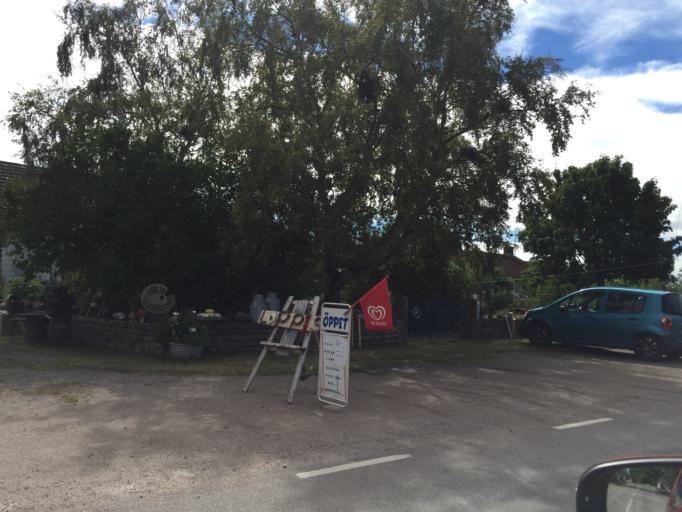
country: SE
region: Kalmar
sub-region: Morbylanga Kommun
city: Sodra Sandby
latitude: 56.5088
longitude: 16.5935
